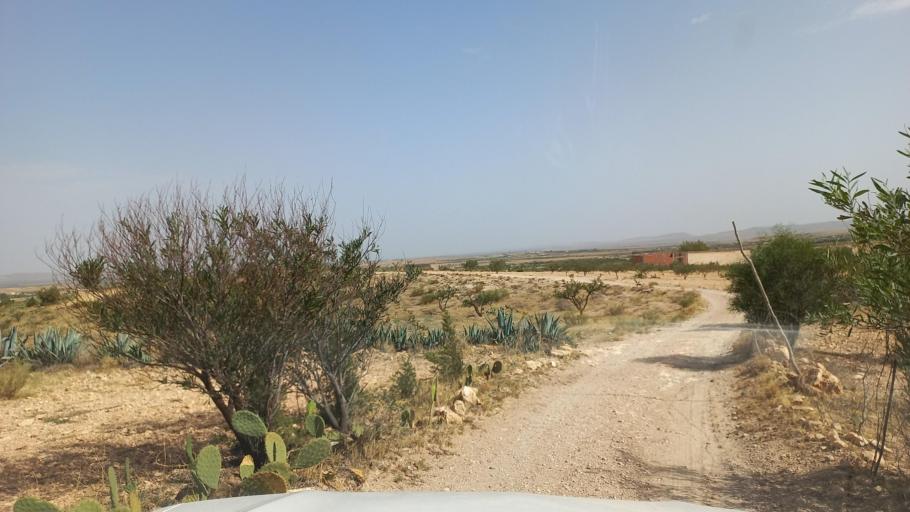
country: TN
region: Al Qasrayn
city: Kasserine
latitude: 35.2998
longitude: 8.9419
